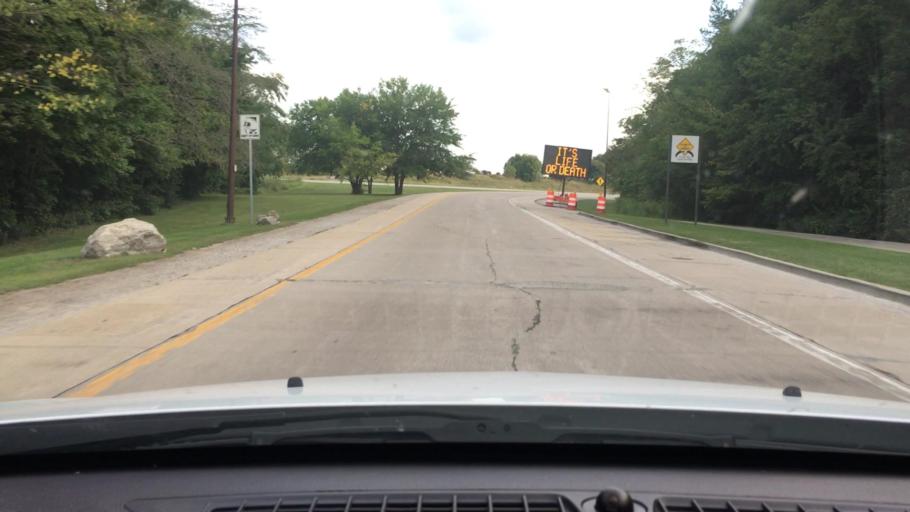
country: US
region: Illinois
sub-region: McLean County
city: Twin Grove
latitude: 40.3577
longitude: -89.1106
